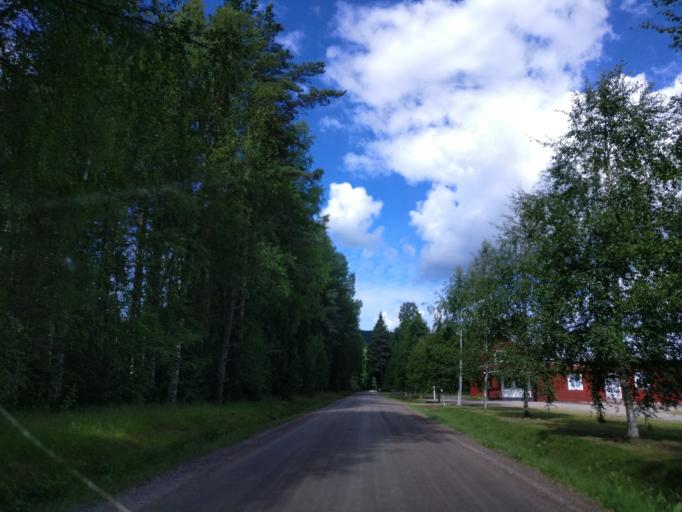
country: SE
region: Vaermland
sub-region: Hagfors Kommun
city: Ekshaerad
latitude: 60.0514
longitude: 13.4840
